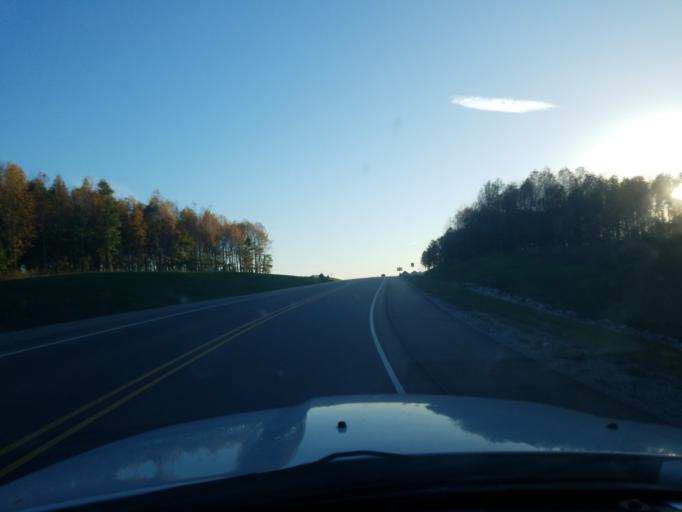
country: US
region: Indiana
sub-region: Floyd County
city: Galena
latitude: 38.4306
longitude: -85.9367
